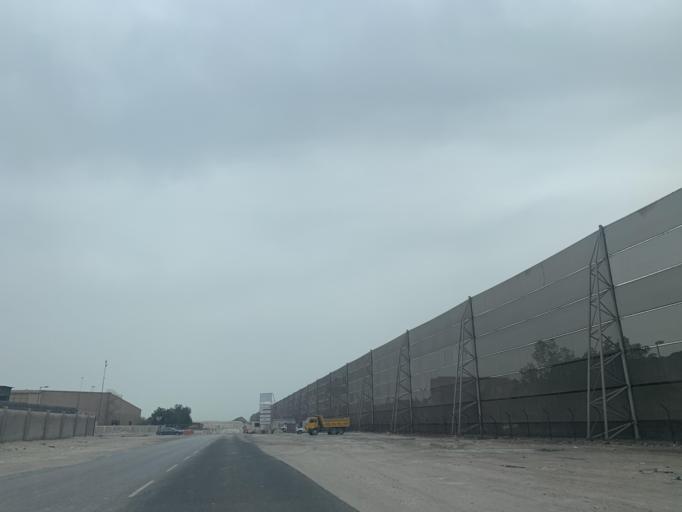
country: BH
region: Muharraq
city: Al Hadd
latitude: 26.2032
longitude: 50.6821
